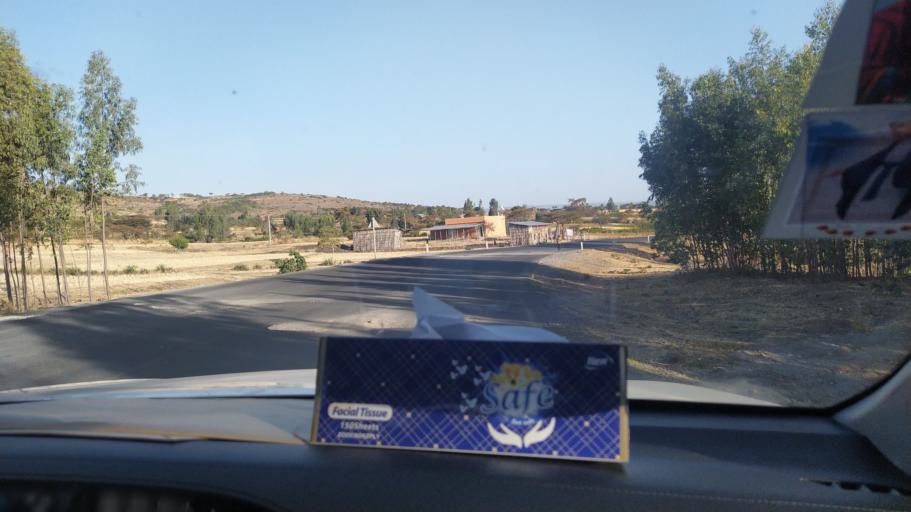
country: ET
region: Southern Nations, Nationalities, and People's Region
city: K'olito
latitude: 7.6988
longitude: 38.1302
